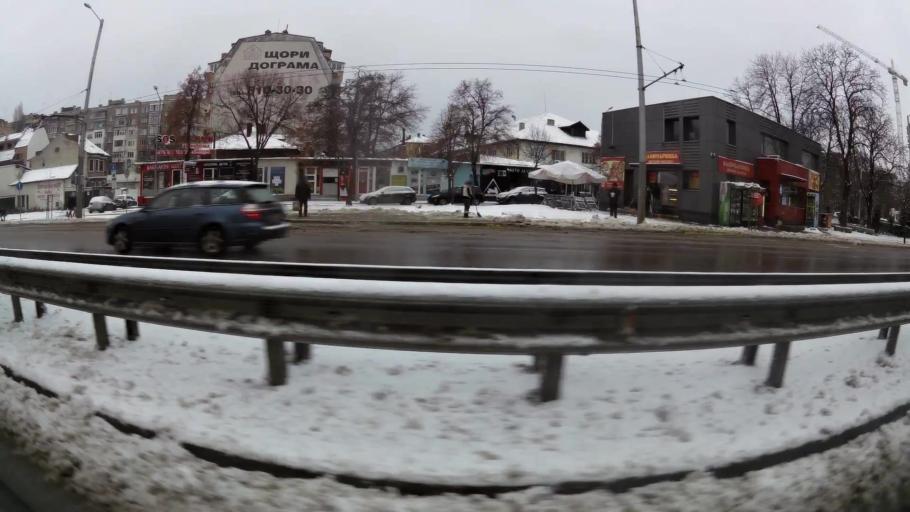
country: BG
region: Sofia-Capital
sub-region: Stolichna Obshtina
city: Sofia
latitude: 42.7069
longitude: 23.2999
